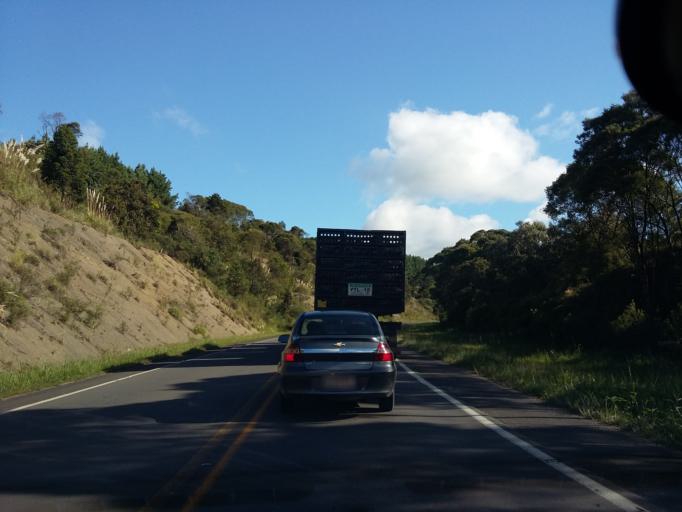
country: BR
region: Santa Catarina
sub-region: Anitapolis
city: Anitapolis
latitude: -27.7792
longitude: -49.4126
